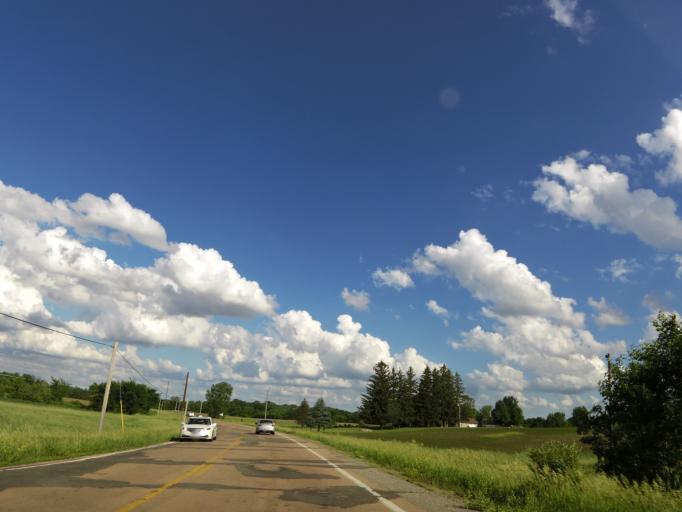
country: US
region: Minnesota
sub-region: Carver County
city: Chaska
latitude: 44.8034
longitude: -93.6411
